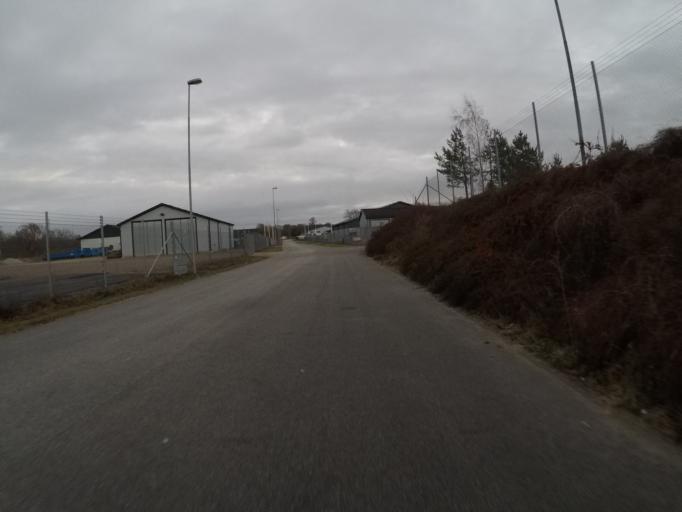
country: SE
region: Skane
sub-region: Sjobo Kommun
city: Sjoebo
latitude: 55.6382
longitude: 13.6862
